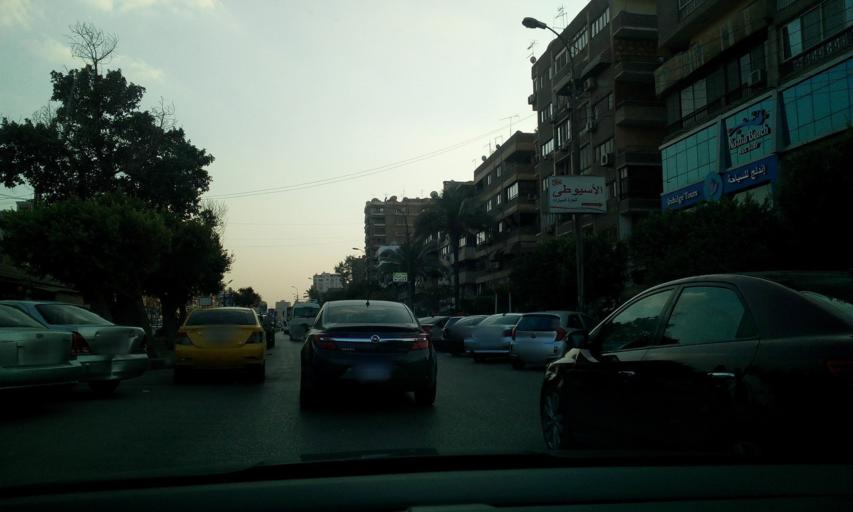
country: EG
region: Muhafazat al Qalyubiyah
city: Al Khankah
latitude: 30.1179
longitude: 31.3553
